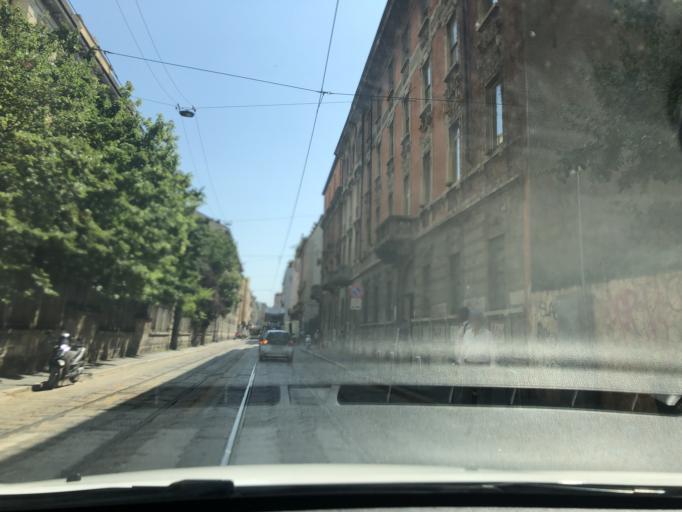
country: IT
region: Lombardy
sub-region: Citta metropolitana di Milano
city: Milano
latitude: 45.4563
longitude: 9.1975
